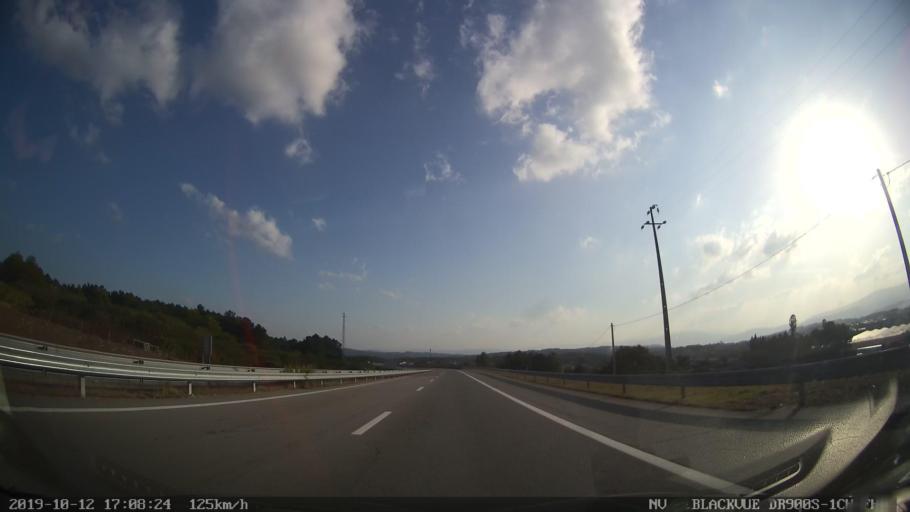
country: PT
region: Vila Real
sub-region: Vila Real
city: Vila Real
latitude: 41.2877
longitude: -7.6906
